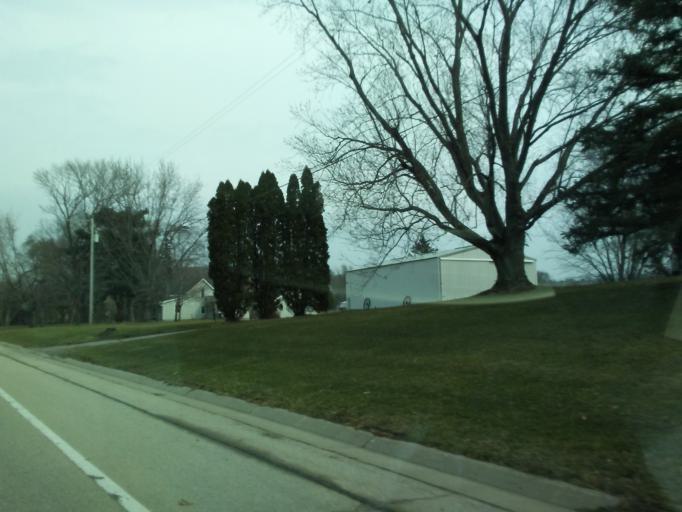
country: US
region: Wisconsin
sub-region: Columbia County
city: Lodi
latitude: 43.2974
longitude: -89.5231
